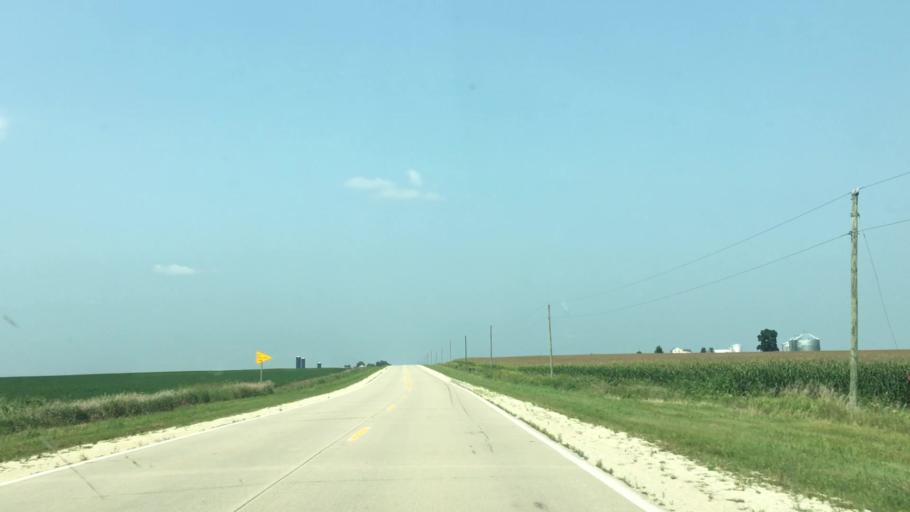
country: US
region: Iowa
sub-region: Fayette County
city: Fayette
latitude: 42.7303
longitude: -91.8040
